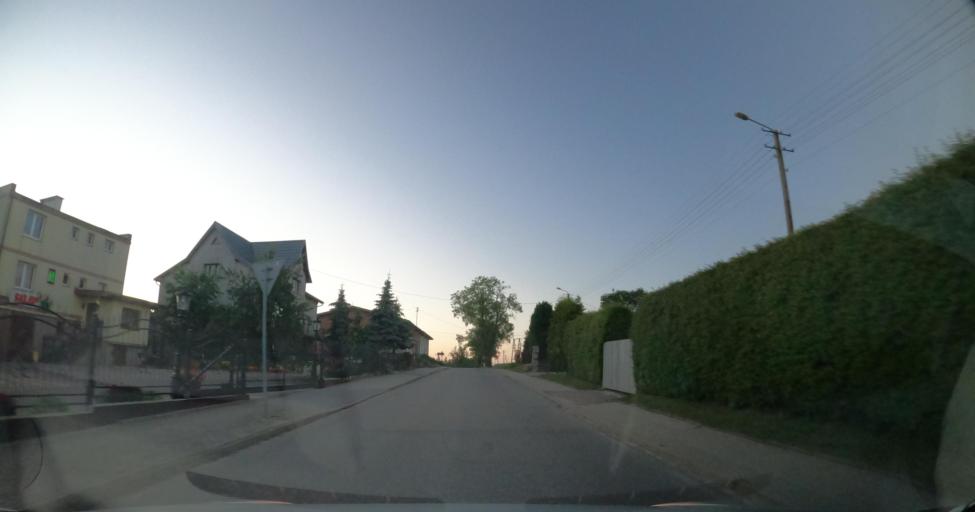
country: PL
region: Pomeranian Voivodeship
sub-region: Powiat wejherowski
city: Szemud
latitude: 54.4628
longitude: 18.1399
